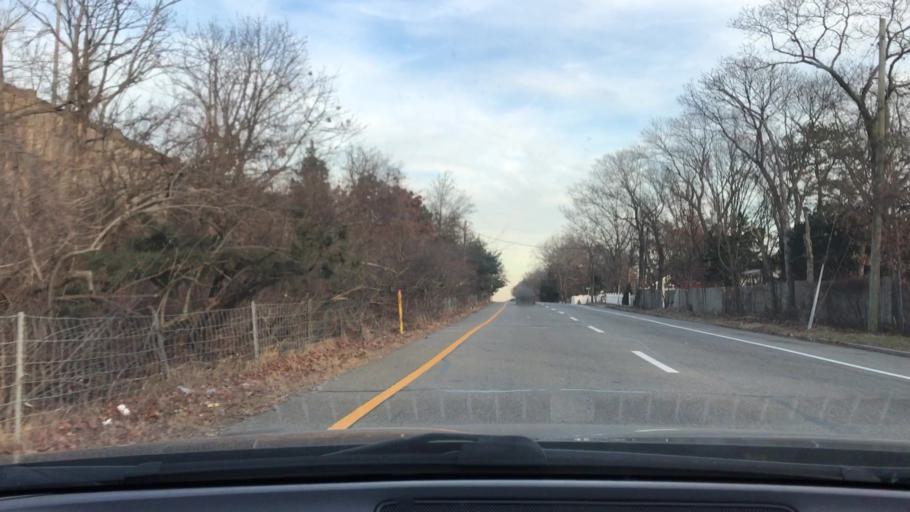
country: US
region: New York
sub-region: Suffolk County
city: Holbrook
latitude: 40.8159
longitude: -73.0777
